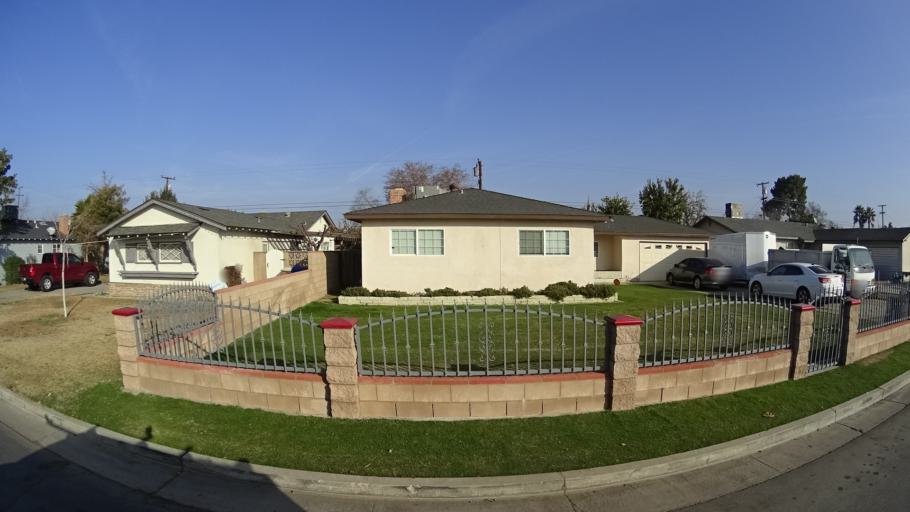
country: US
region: California
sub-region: Kern County
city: Bakersfield
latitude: 35.3362
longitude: -119.0273
